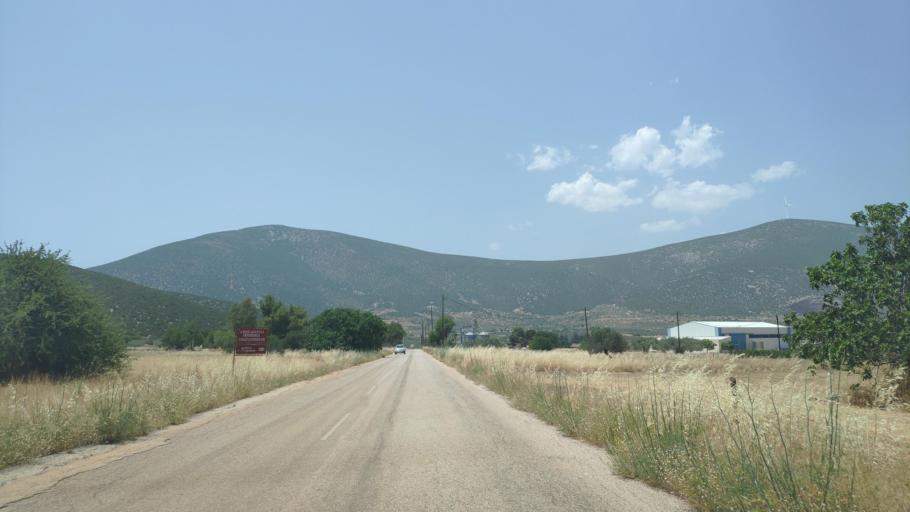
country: GR
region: Peloponnese
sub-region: Nomos Argolidos
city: Didyma
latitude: 37.4526
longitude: 23.1741
